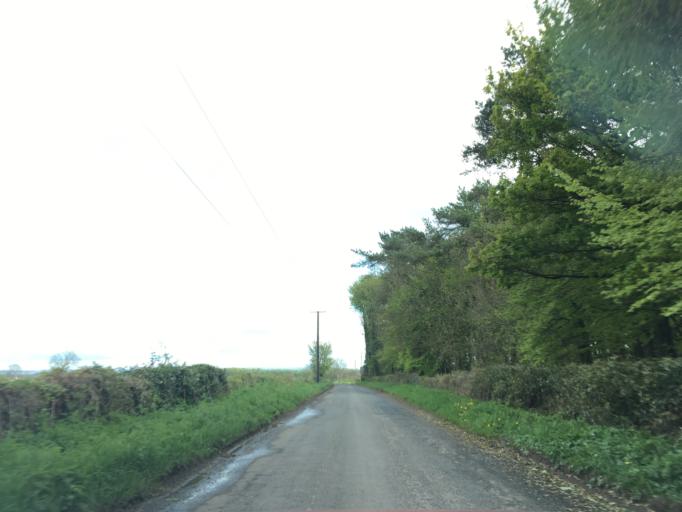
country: GB
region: England
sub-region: Wiltshire
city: Luckington
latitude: 51.5881
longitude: -2.2924
